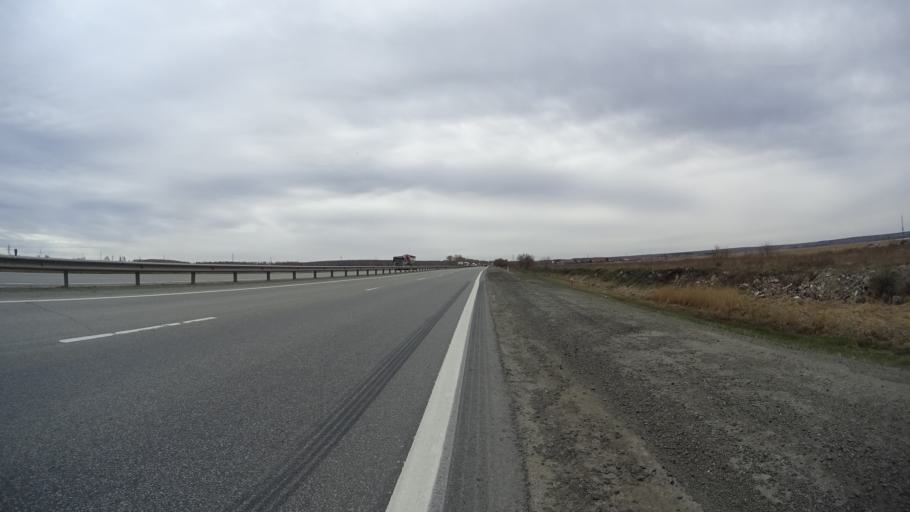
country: RU
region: Chelyabinsk
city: Roza
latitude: 54.9893
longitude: 61.4414
